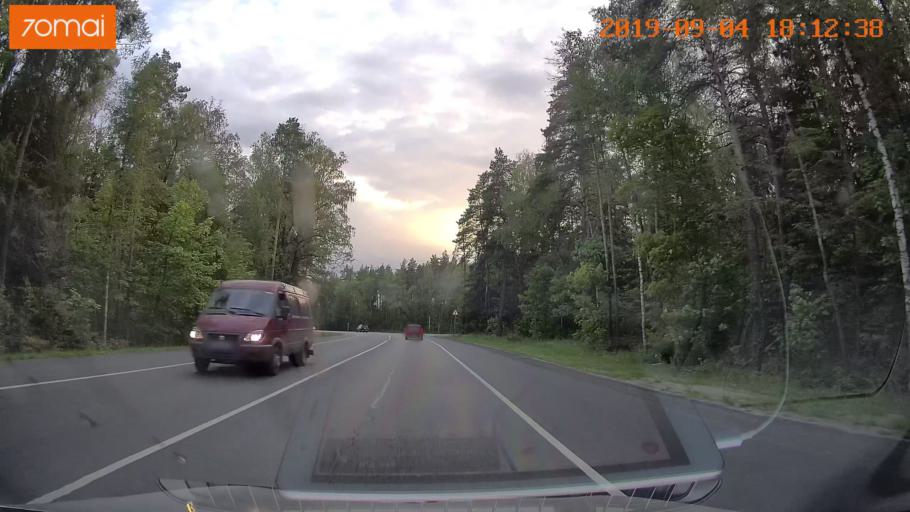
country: RU
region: Moskovskaya
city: Lopatinskiy
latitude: 55.3689
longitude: 38.7390
